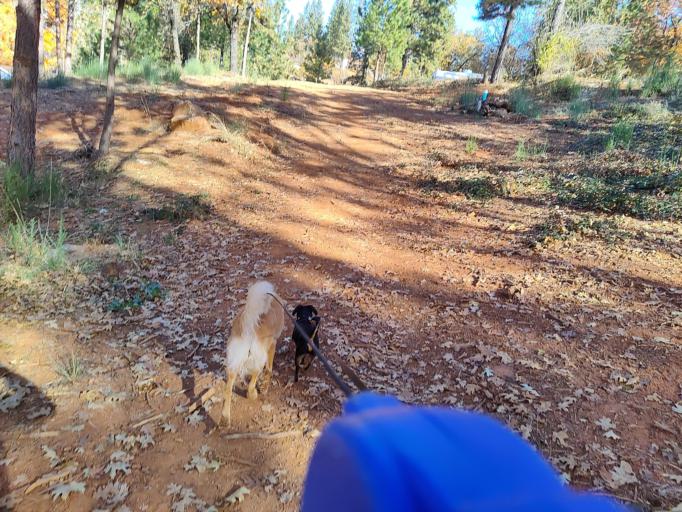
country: US
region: California
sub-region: Placer County
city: Meadow Vista
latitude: 39.0366
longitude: -120.9791
